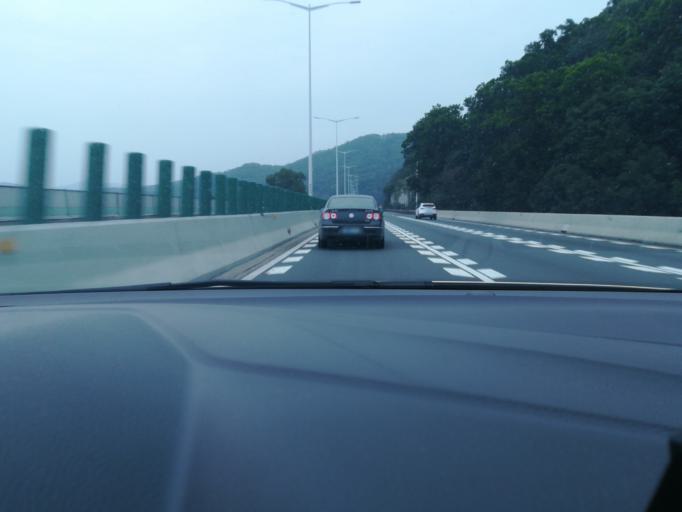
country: CN
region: Guangdong
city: Longdong
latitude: 23.2426
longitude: 113.3517
